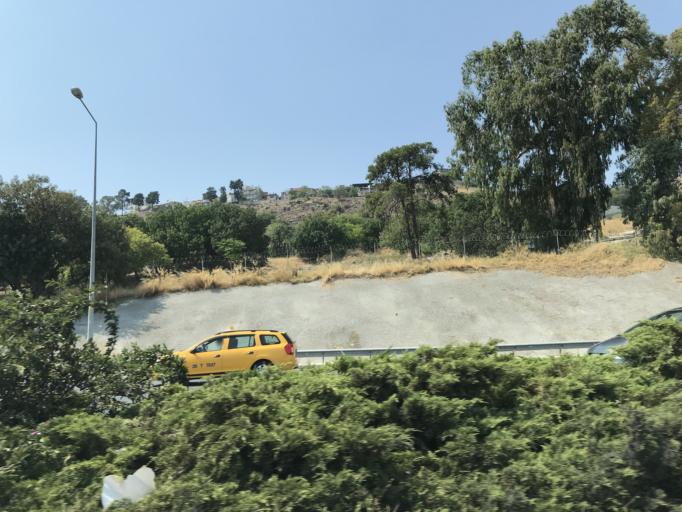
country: TR
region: Izmir
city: Izmir
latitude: 38.3998
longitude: 27.1404
